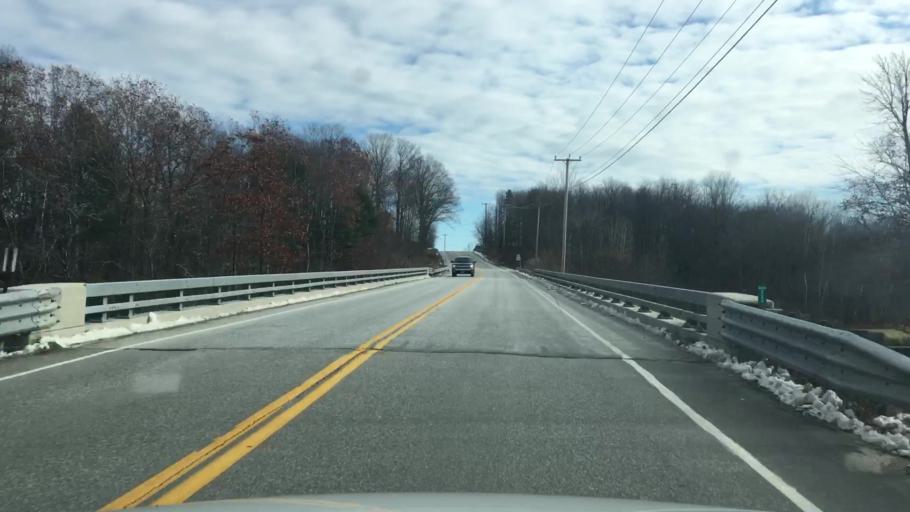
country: US
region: Maine
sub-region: Androscoggin County
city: Leeds
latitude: 44.3455
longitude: -70.1503
